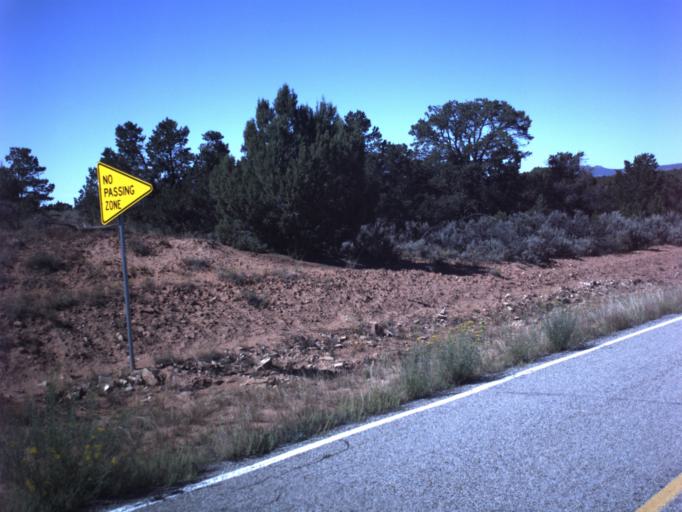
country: US
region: Utah
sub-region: San Juan County
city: Blanding
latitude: 37.4571
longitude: -109.9159
